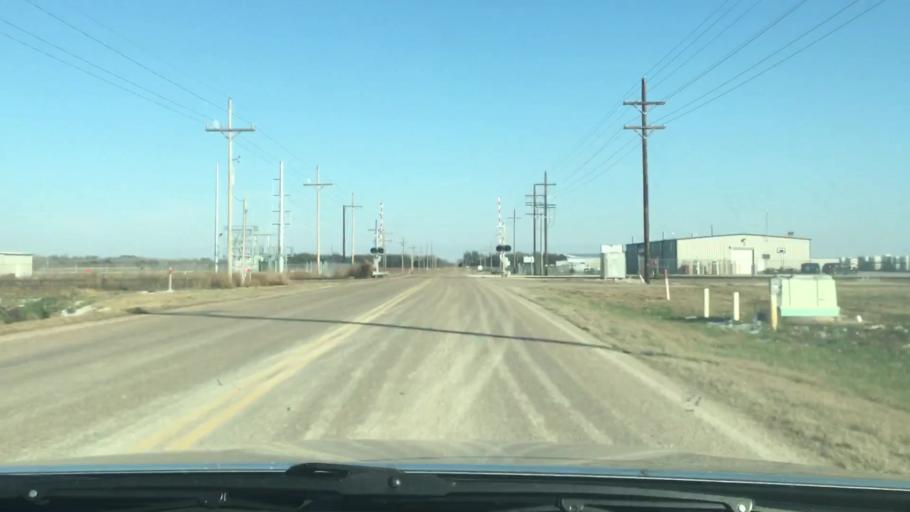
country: US
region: Kansas
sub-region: Rice County
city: Lyons
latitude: 38.2895
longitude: -98.1938
